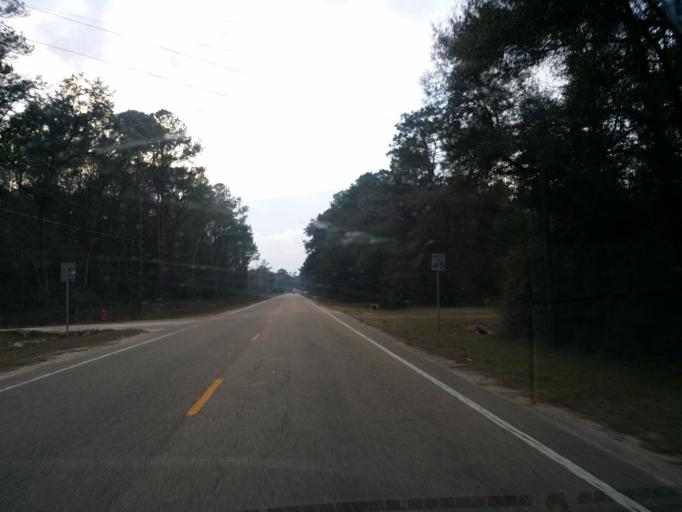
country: US
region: Florida
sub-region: Leon County
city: Woodville
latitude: 30.2292
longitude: -84.2219
